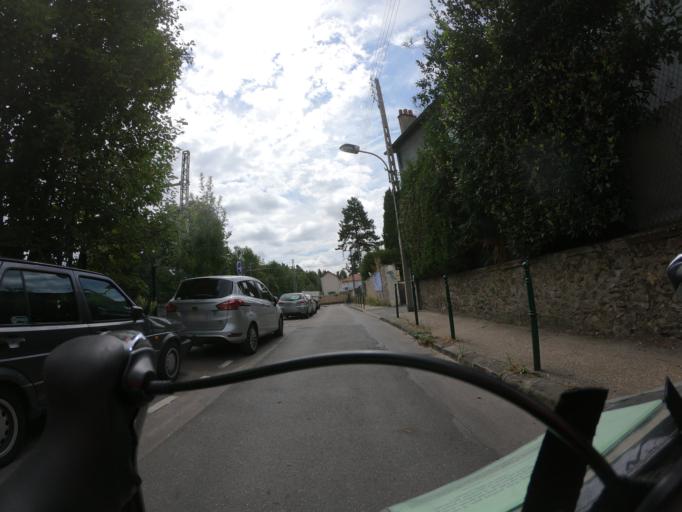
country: FR
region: Ile-de-France
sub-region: Departement de l'Essonne
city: Igny
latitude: 48.7445
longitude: 2.2285
